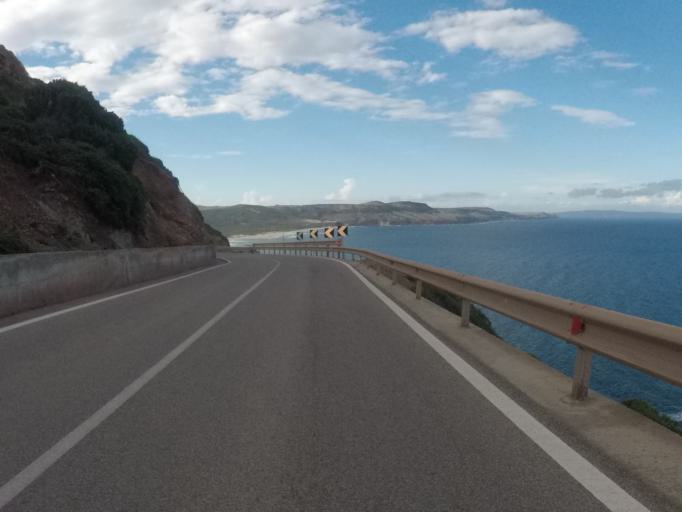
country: IT
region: Sardinia
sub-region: Provincia di Carbonia-Iglesias
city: Gonnesa
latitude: 39.3010
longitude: 8.4359
